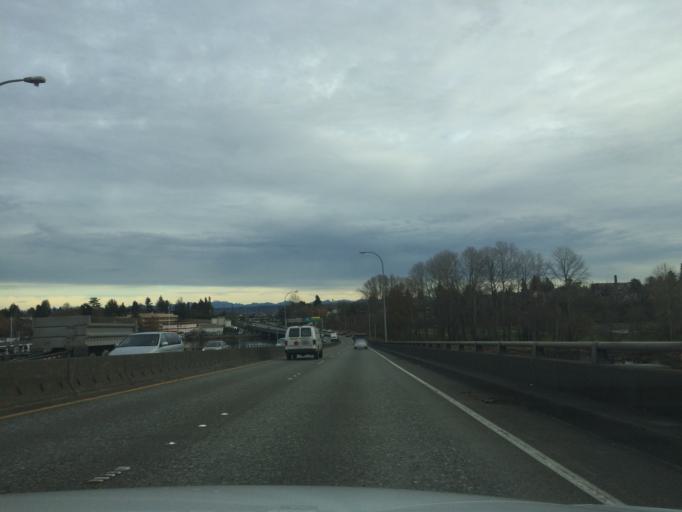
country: US
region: Washington
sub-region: King County
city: Seattle
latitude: 47.6431
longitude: -122.3133
